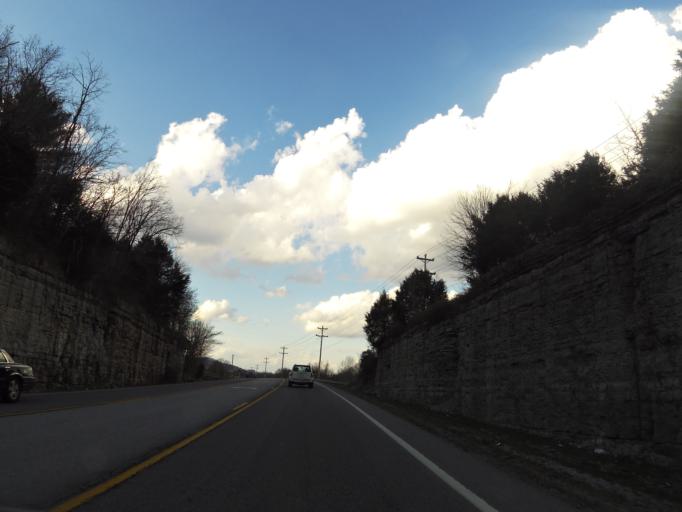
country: US
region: Tennessee
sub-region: Smith County
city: South Carthage
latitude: 36.2089
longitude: -85.9521
